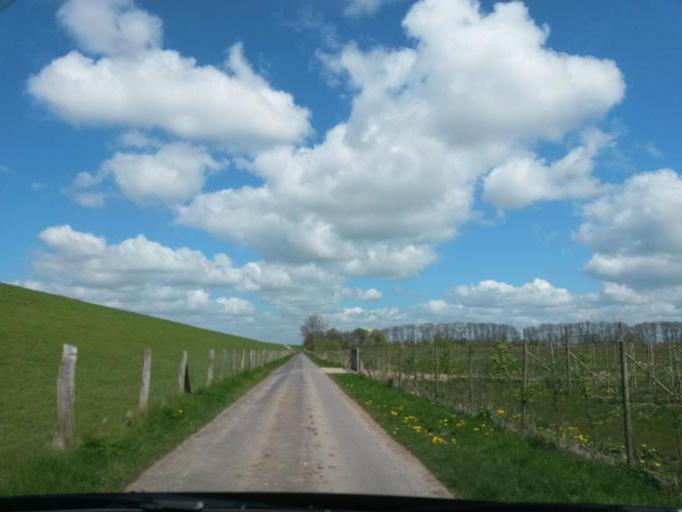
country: DE
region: Schleswig-Holstein
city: Seestermuhe
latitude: 53.6593
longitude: 9.5568
